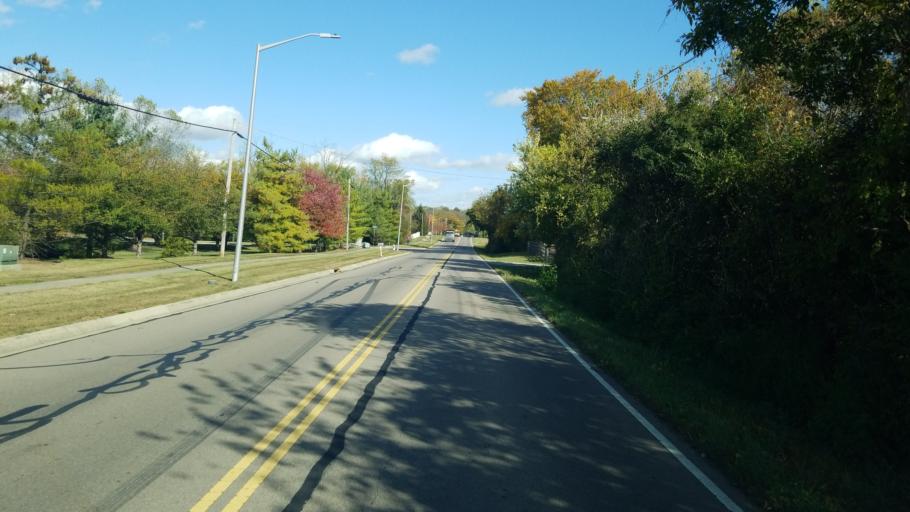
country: US
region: Ohio
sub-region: Warren County
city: Lebanon
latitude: 39.4264
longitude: -84.1879
